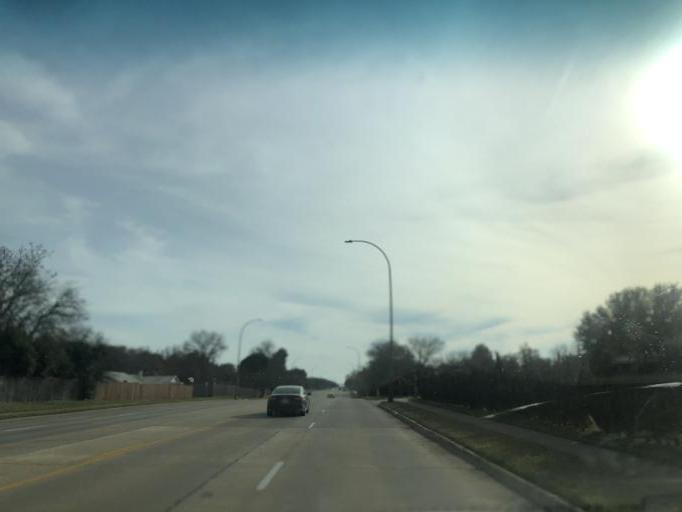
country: US
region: Texas
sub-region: Tarrant County
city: Dalworthington Gardens
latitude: 32.6967
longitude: -97.1494
